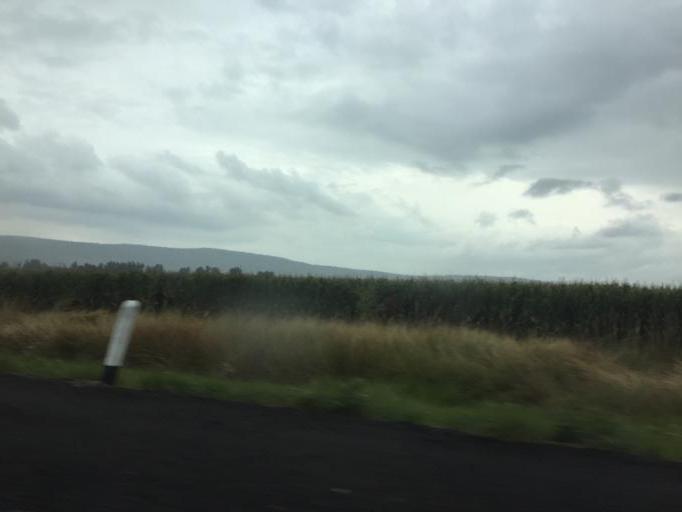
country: MX
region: Jalisco
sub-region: Zapotlan del Rey
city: Zapotlan del Rey
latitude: 20.4508
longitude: -102.8842
